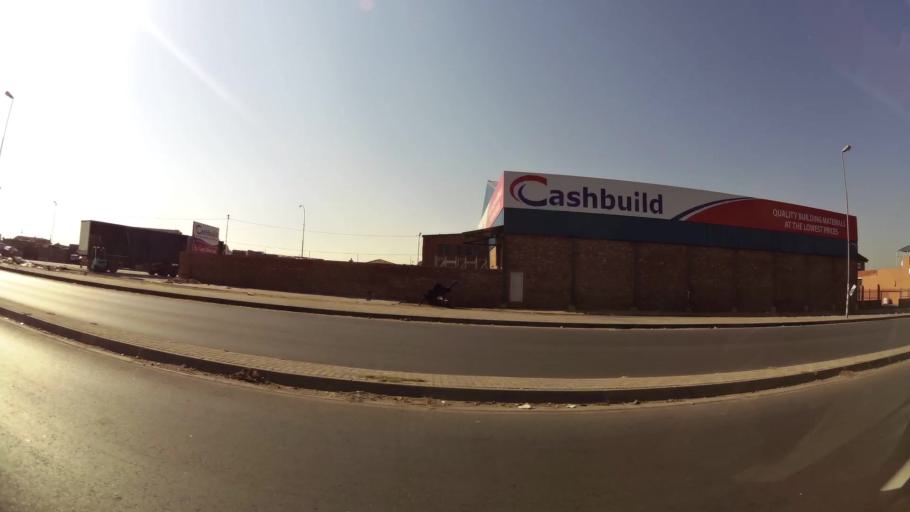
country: ZA
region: Gauteng
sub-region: City of Johannesburg Metropolitan Municipality
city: Modderfontein
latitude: -26.1035
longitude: 28.0855
